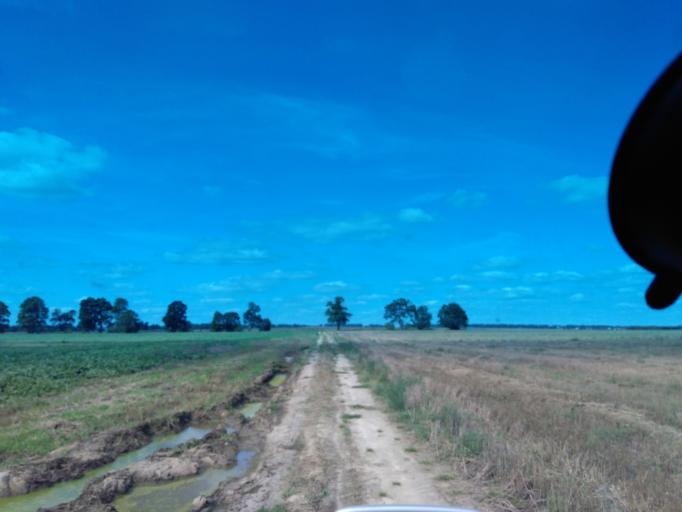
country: BY
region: Minsk
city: Stan'kava
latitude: 53.6321
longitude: 27.3264
